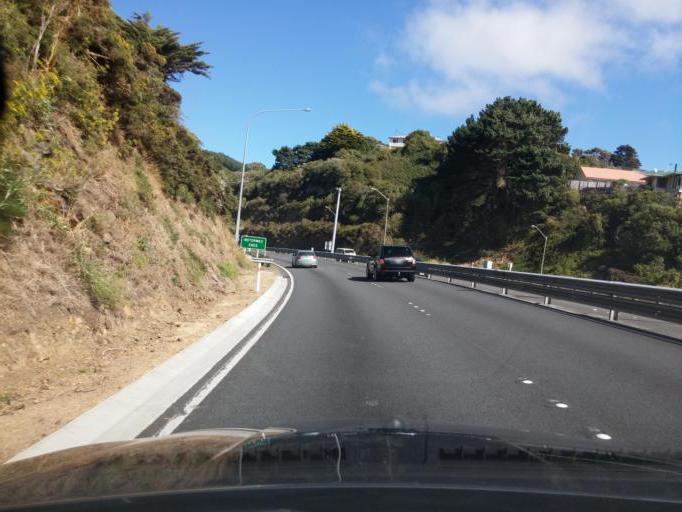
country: NZ
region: Wellington
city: Petone
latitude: -41.2270
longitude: 174.8081
